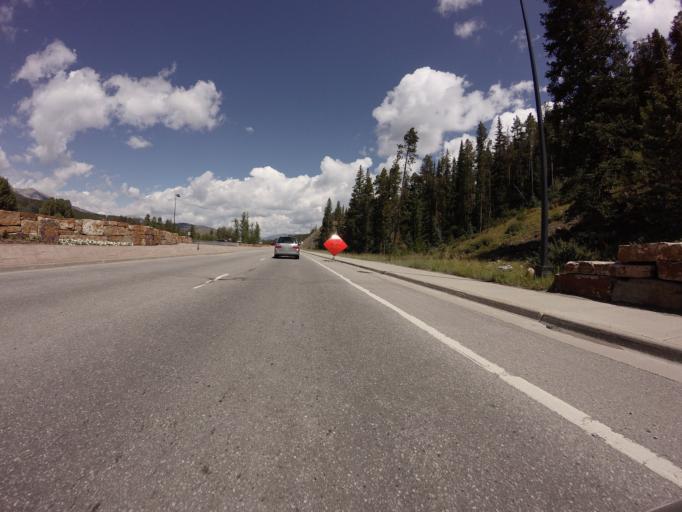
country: US
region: Colorado
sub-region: Summit County
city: Breckenridge
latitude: 39.4912
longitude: -106.0455
